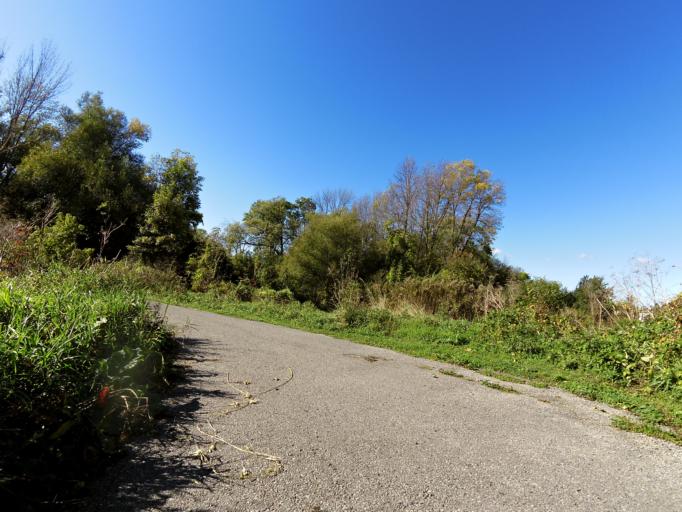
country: CA
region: Ontario
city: Oshawa
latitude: 43.8576
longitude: -78.8881
